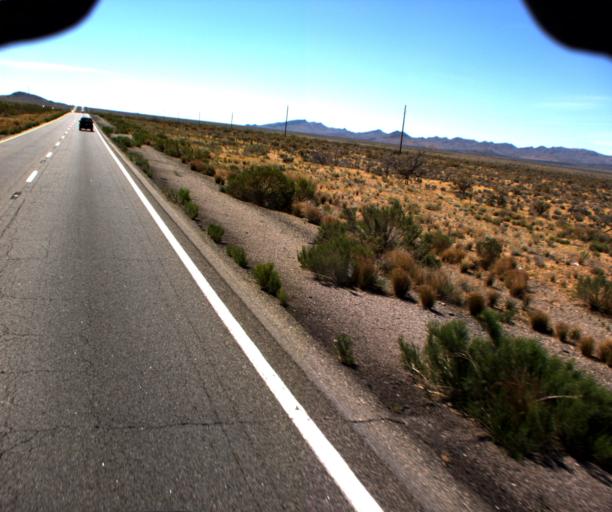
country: US
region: Arizona
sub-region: Mohave County
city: Dolan Springs
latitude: 35.4725
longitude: -114.3131
